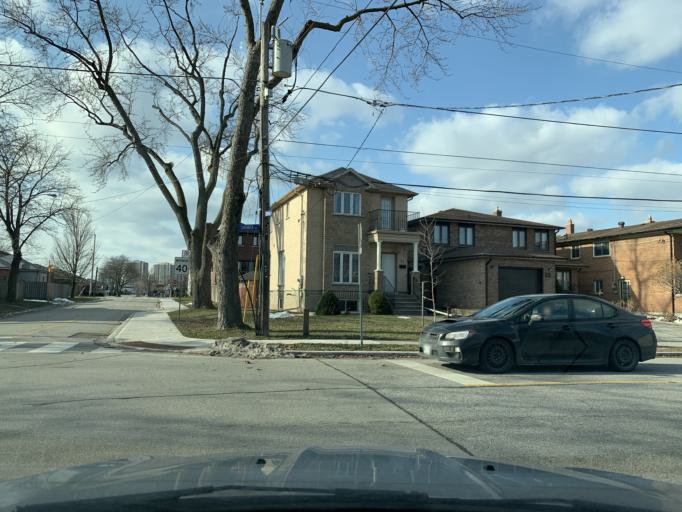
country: CA
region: Ontario
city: Toronto
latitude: 43.7027
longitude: -79.4972
